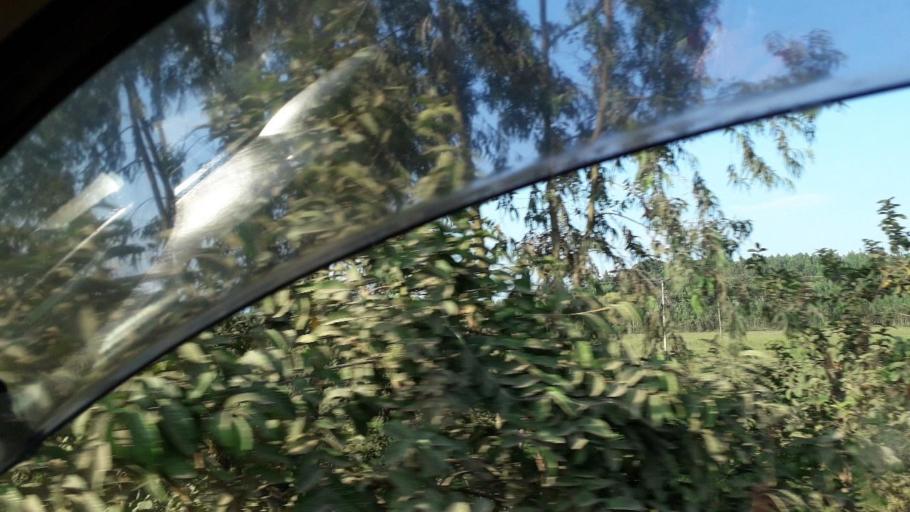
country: ET
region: Oromiya
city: Jima
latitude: 7.5944
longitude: 36.8507
